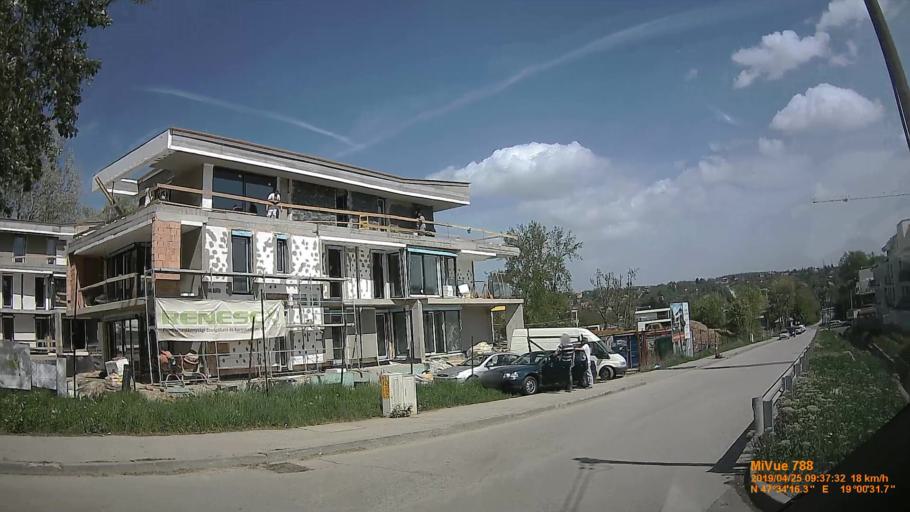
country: HU
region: Pest
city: Urom
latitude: 47.5713
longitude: 19.0089
